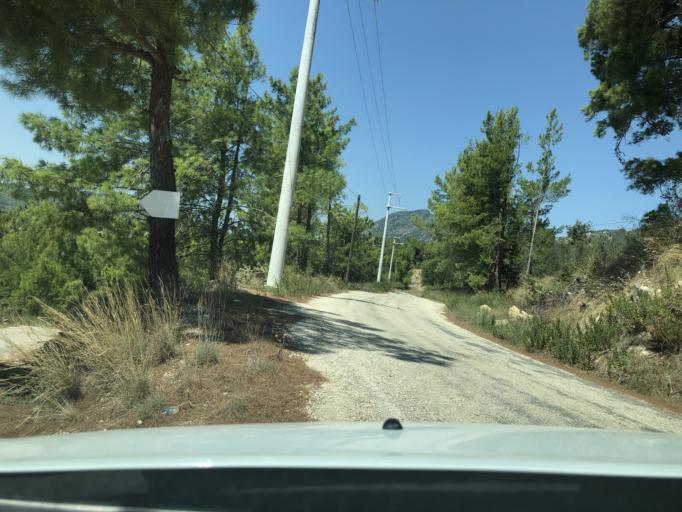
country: TR
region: Antalya
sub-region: Manavgat
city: Manavgat
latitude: 36.8720
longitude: 31.5518
